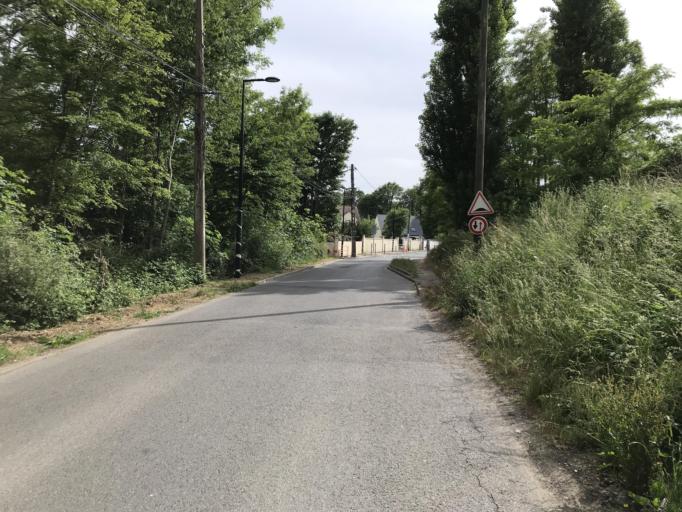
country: FR
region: Ile-de-France
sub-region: Departement de l'Essonne
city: La Ville-du-Bois
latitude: 48.6545
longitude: 2.2565
